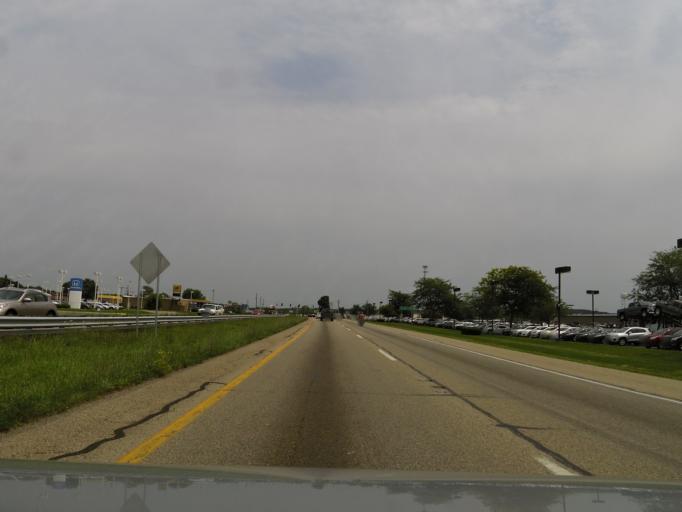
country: US
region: Ohio
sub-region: Greene County
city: Beavercreek
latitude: 39.7071
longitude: -84.0229
